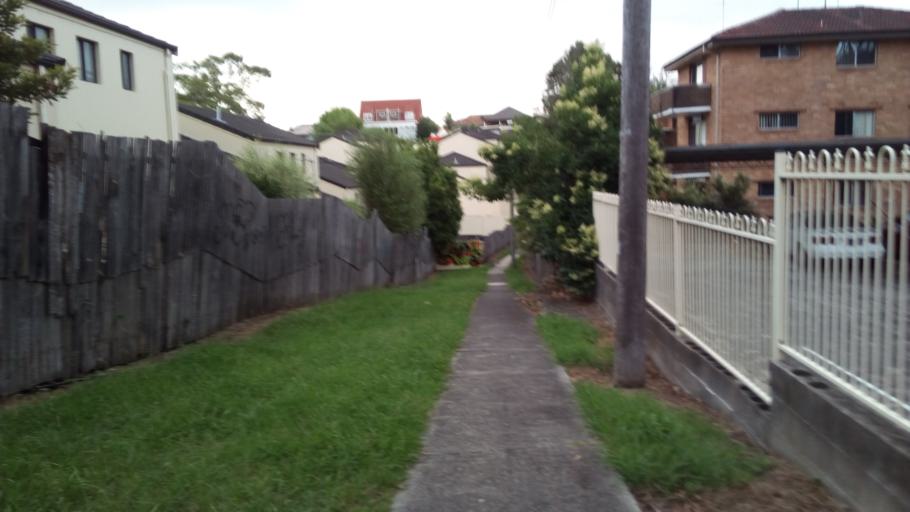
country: AU
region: New South Wales
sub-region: Wollongong
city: West Wollongong
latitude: -34.4269
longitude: 150.8735
